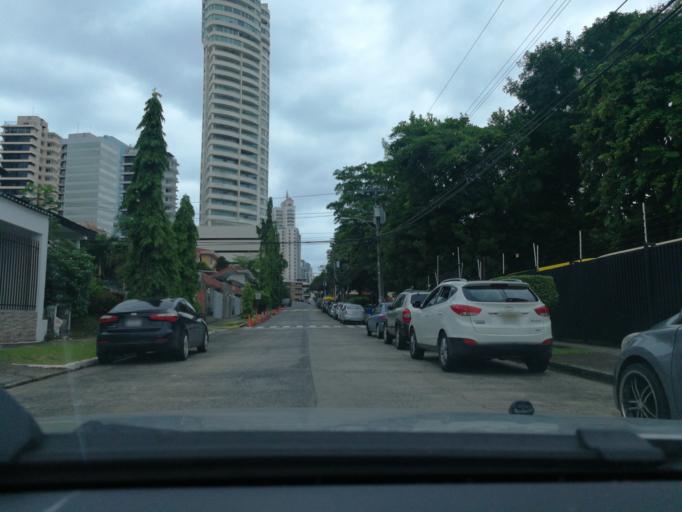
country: PA
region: Panama
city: Panama
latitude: 8.9953
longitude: -79.5221
